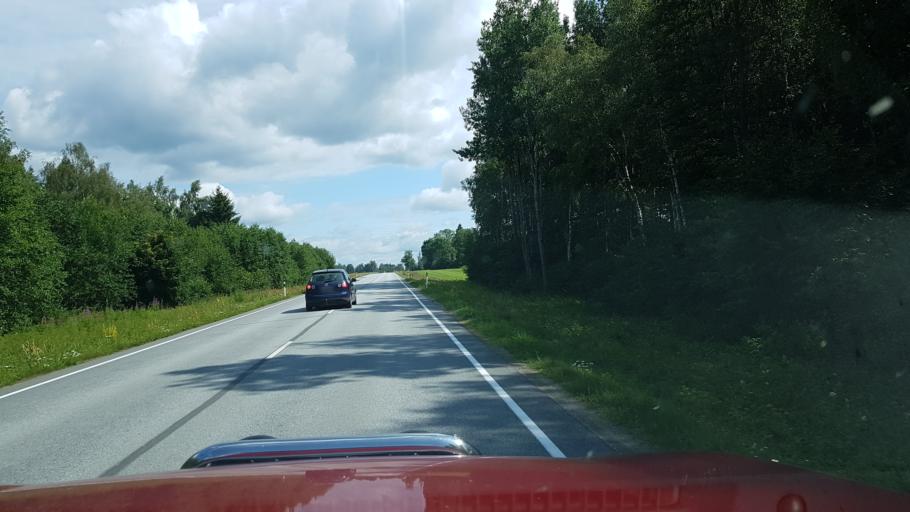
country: EE
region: Jogevamaa
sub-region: Jogeva linn
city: Jogeva
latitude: 58.8186
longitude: 26.5718
